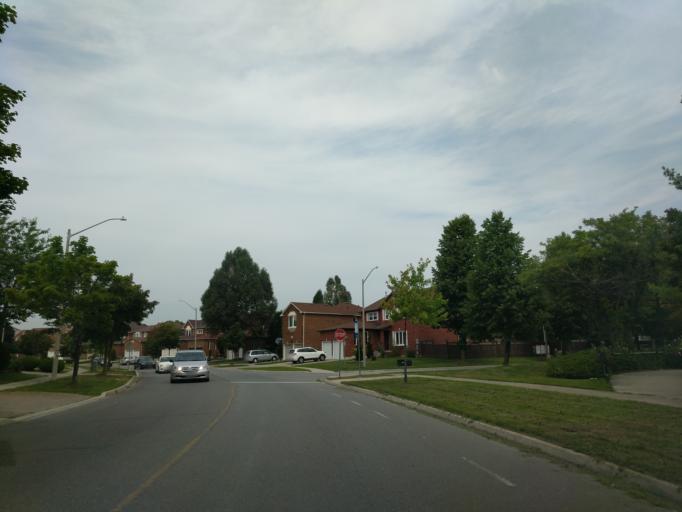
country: CA
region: Ontario
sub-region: York
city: Richmond Hill
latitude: 43.8455
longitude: -79.3928
